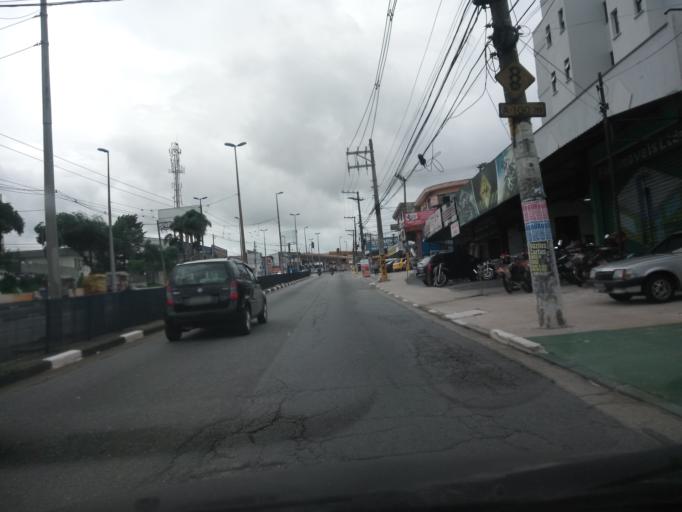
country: BR
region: Sao Paulo
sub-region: Sao Bernardo Do Campo
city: Sao Bernardo do Campo
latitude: -23.6914
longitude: -46.5866
